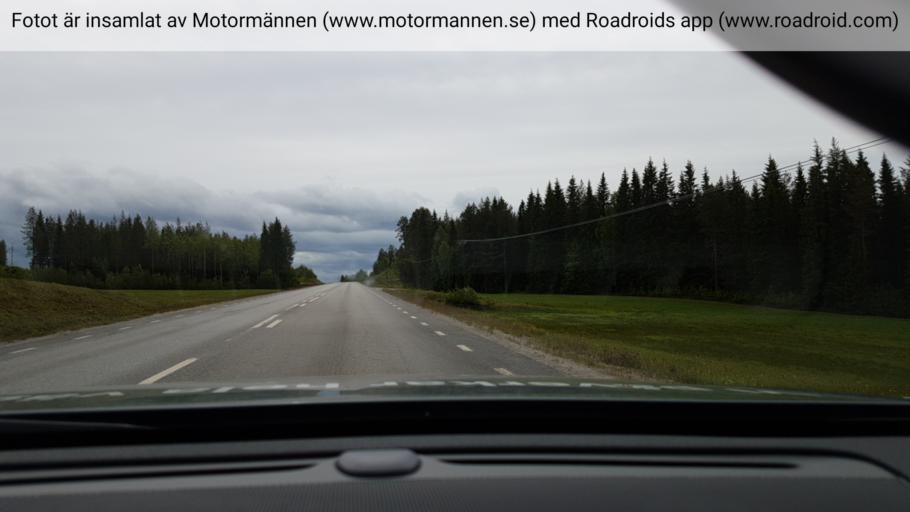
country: SE
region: Vaesterbotten
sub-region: Vannas Kommun
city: Vaennaes
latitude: 64.0366
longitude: 19.6922
